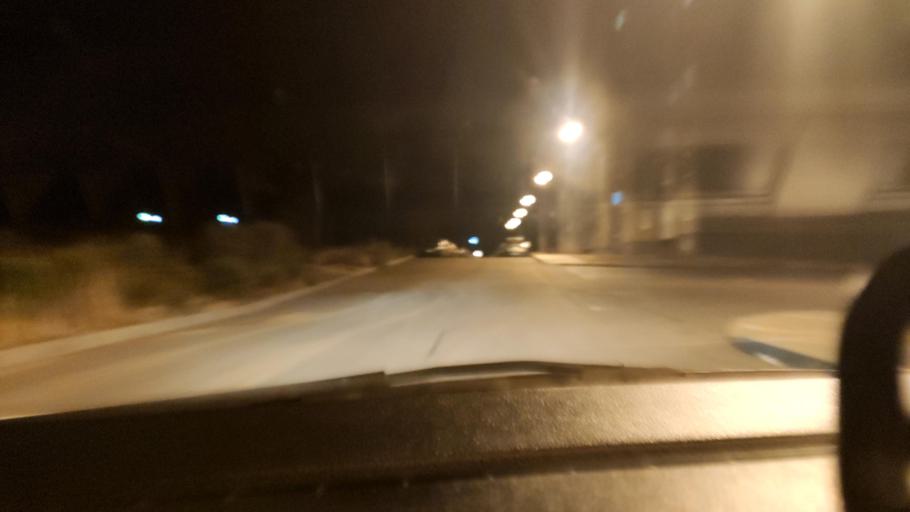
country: RU
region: Voronezj
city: Shilovo
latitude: 51.5746
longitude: 39.1287
